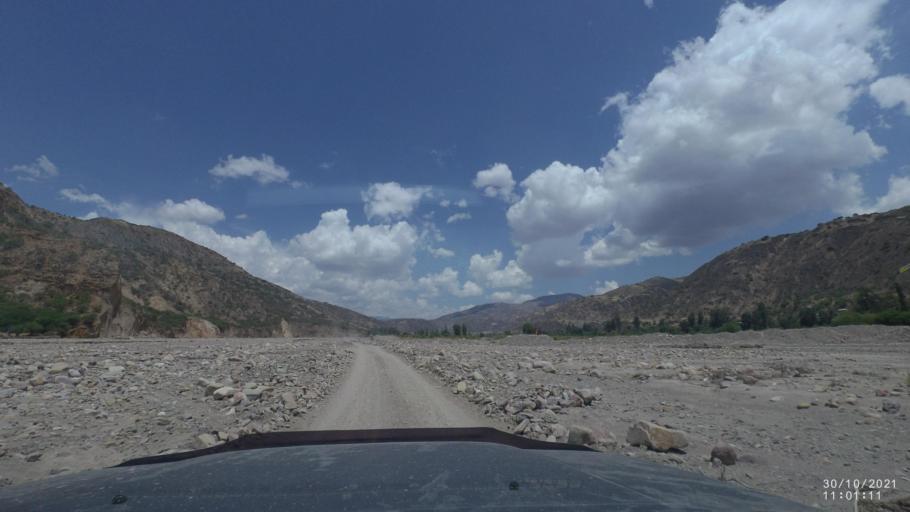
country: BO
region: Cochabamba
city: Sipe Sipe
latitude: -17.5347
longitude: -66.5195
